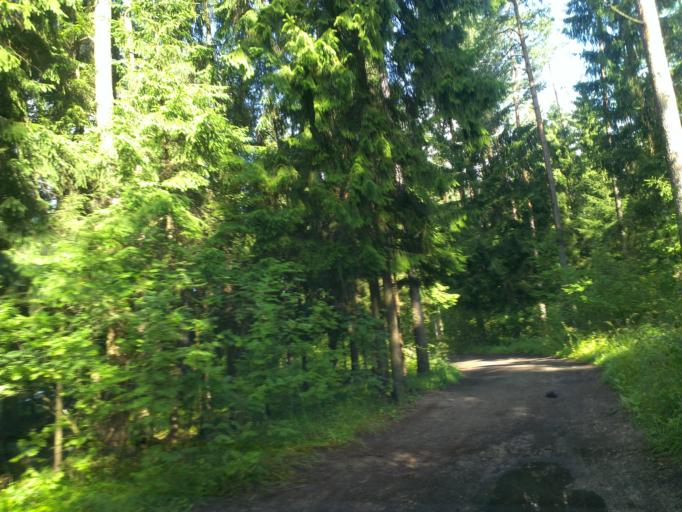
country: LV
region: Incukalns
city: Vangazi
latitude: 57.0967
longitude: 24.5433
